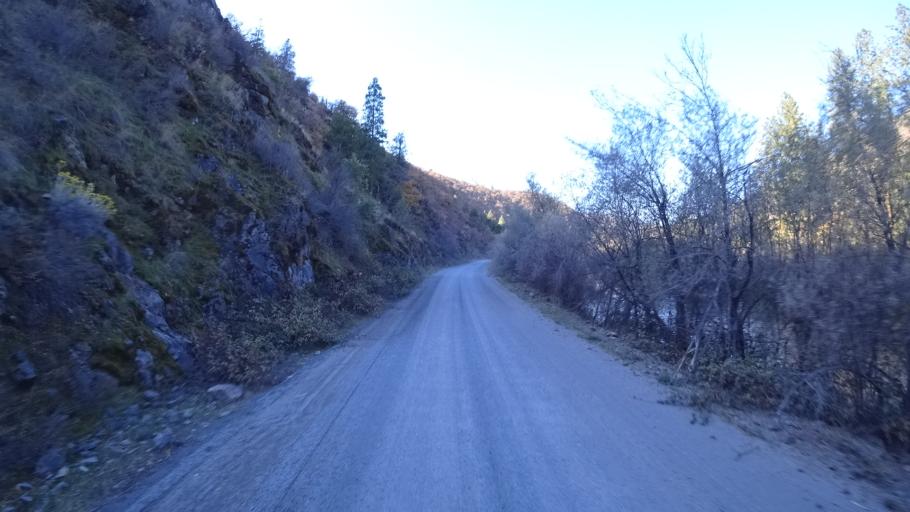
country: US
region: California
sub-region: Siskiyou County
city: Yreka
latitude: 41.8271
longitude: -122.6445
